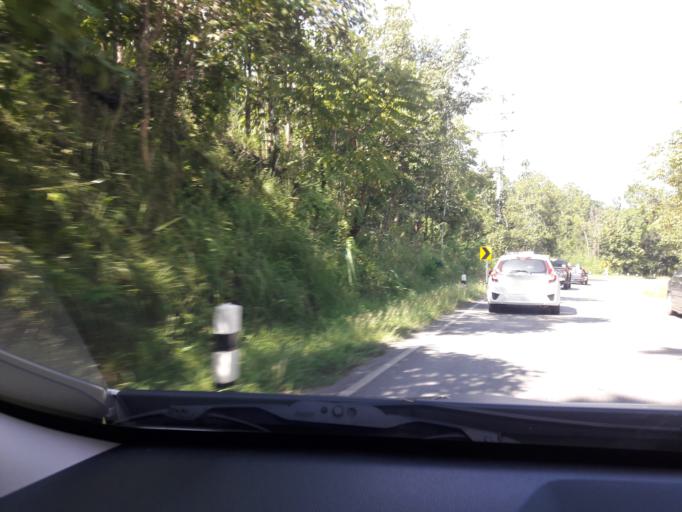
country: TH
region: Mae Hong Son
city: Mae Hi
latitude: 19.3080
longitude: 98.4526
